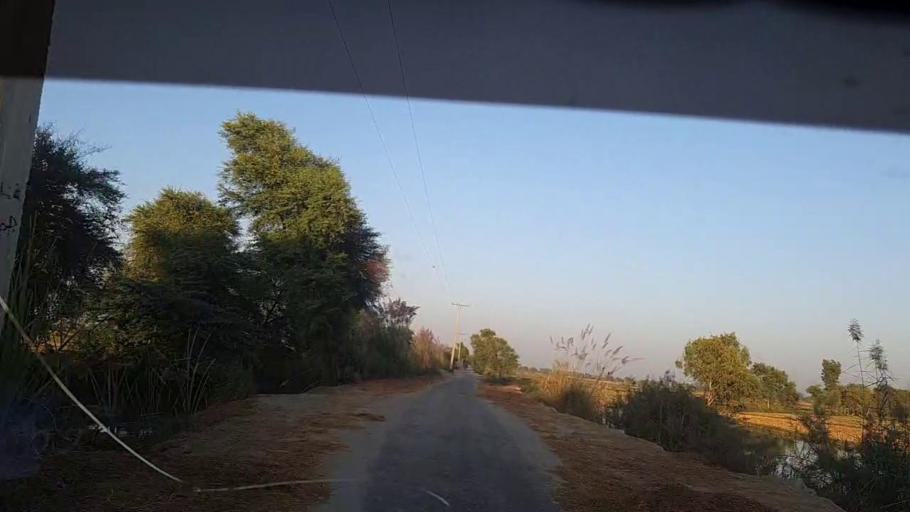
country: PK
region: Sindh
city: Ratodero
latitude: 27.8967
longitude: 68.2281
